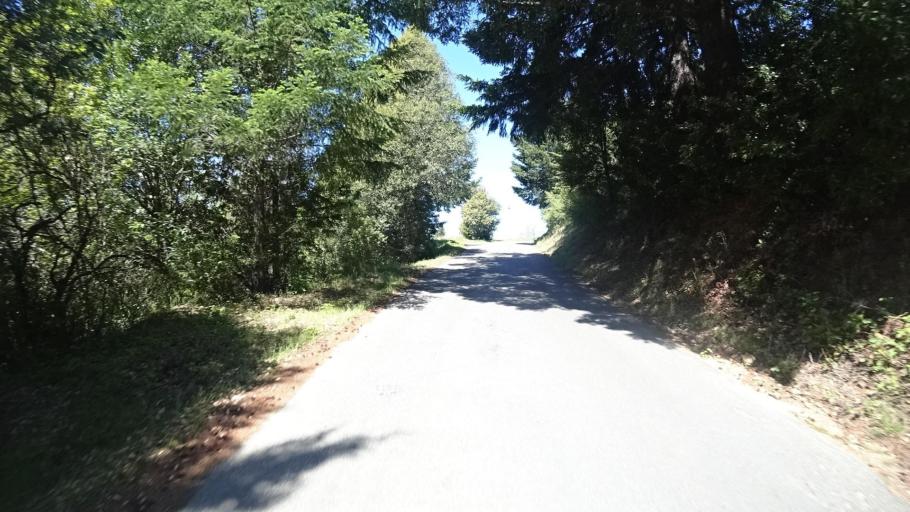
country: US
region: California
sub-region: Humboldt County
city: Redway
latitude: 40.1165
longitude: -123.9682
